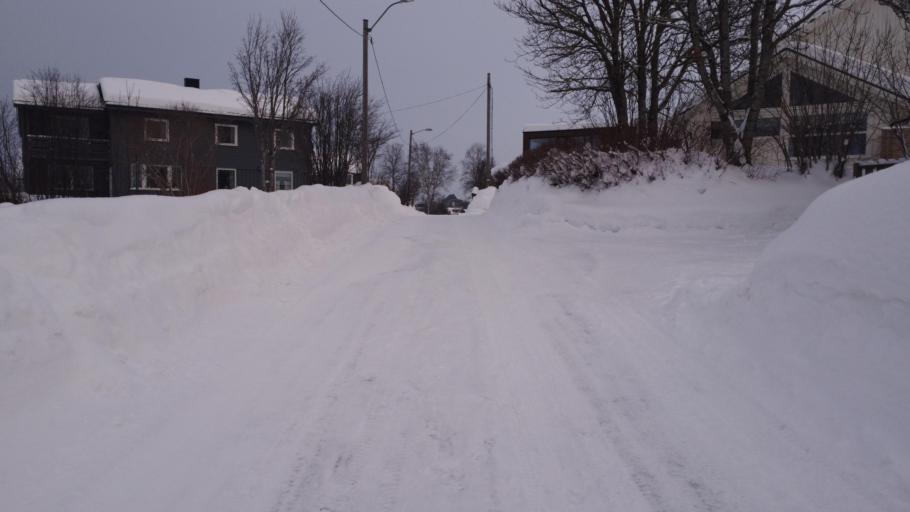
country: NO
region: Nordland
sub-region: Rana
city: Mo i Rana
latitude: 66.3152
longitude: 14.1420
